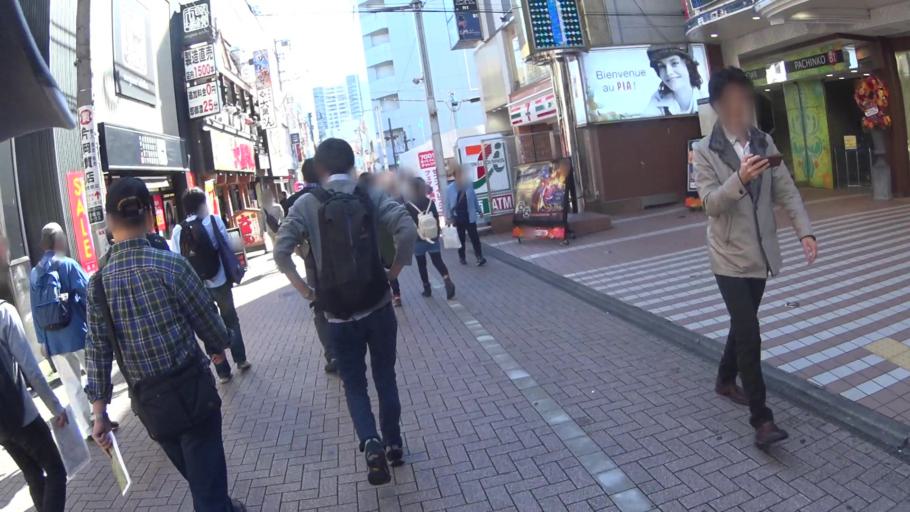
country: JP
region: Tokyo
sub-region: Machida-shi
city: Machida
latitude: 35.5437
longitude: 139.4468
